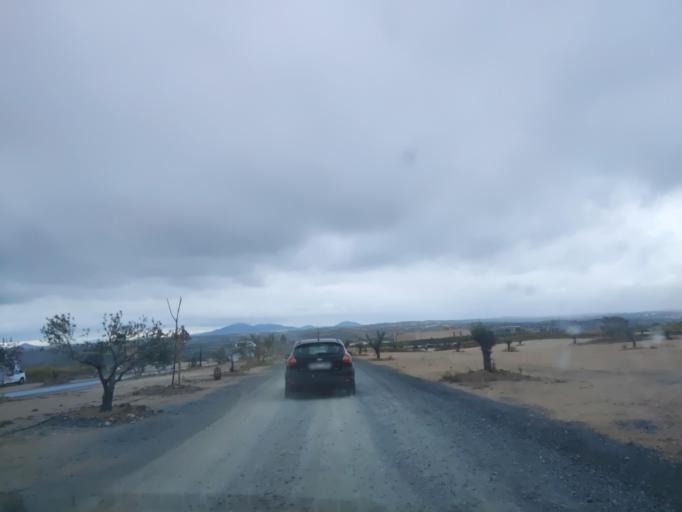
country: ES
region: Castille-La Mancha
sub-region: Province of Toledo
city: Toledo
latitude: 39.8398
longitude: -4.0845
